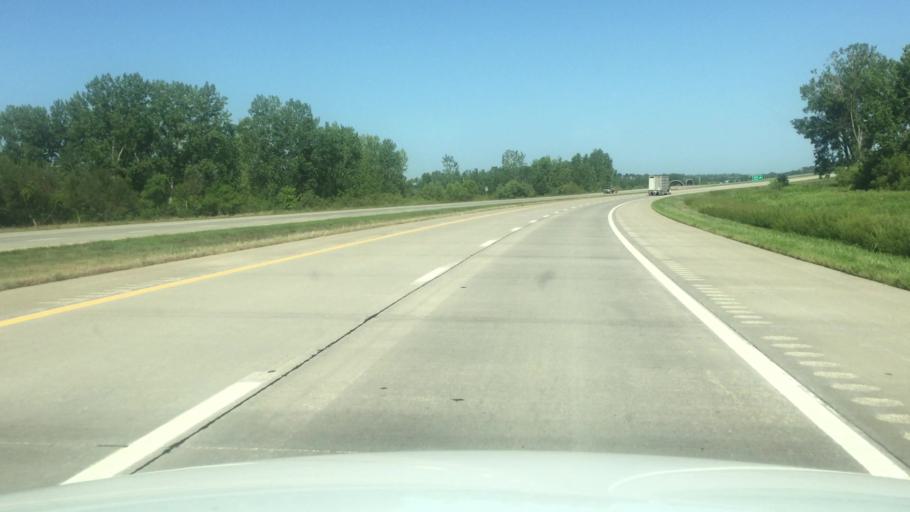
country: US
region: Kansas
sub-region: Doniphan County
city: Wathena
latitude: 39.7417
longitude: -94.9178
